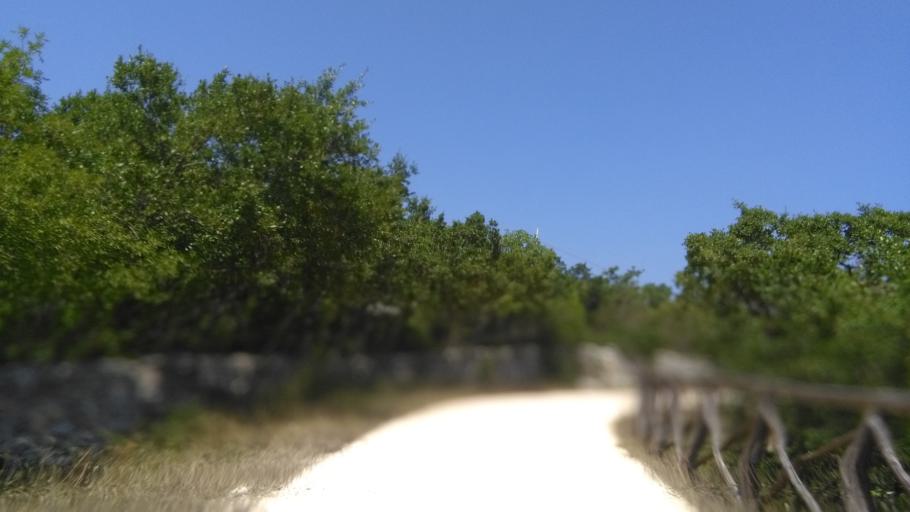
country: IT
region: Apulia
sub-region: Provincia di Brindisi
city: Cisternino
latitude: 40.6806
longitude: 17.4311
